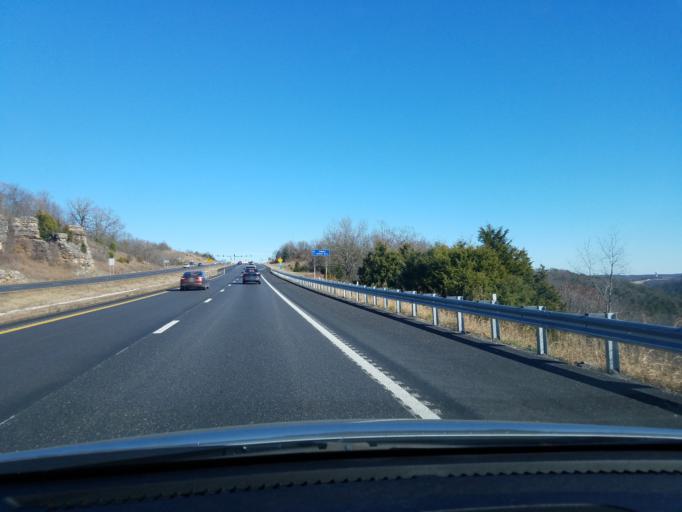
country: US
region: Missouri
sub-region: Taney County
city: Hollister
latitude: 36.5668
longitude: -93.2527
